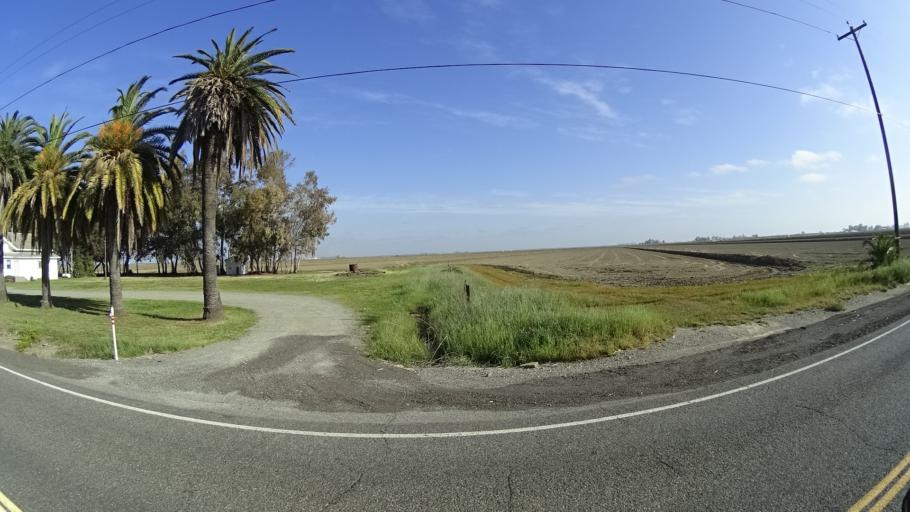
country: US
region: California
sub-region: Glenn County
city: Willows
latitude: 39.5820
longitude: -122.1062
